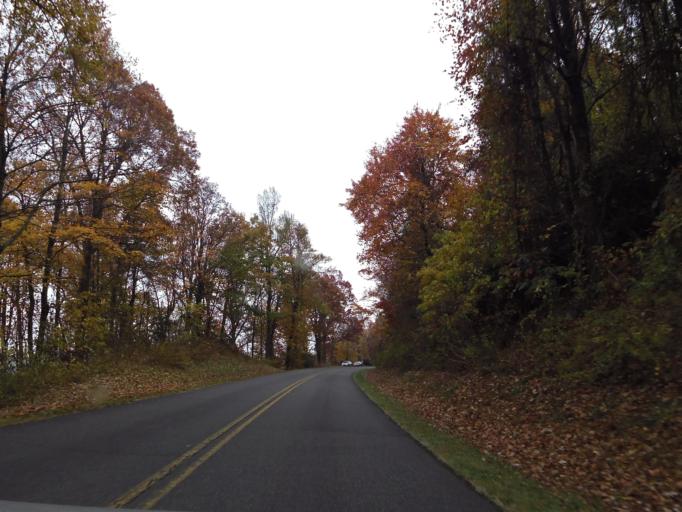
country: US
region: North Carolina
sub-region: Ashe County
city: West Jefferson
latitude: 36.2830
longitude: -81.4131
